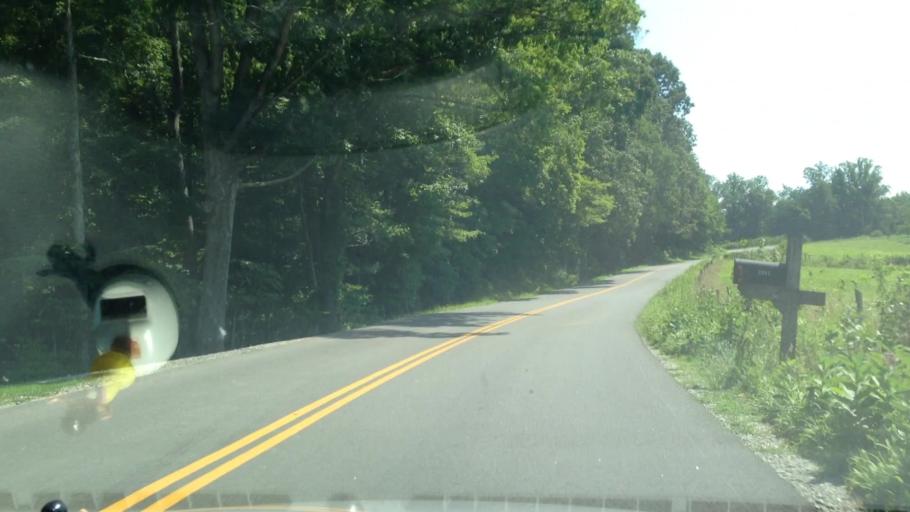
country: US
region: Virginia
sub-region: Patrick County
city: Patrick Springs
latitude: 36.5752
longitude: -80.1948
